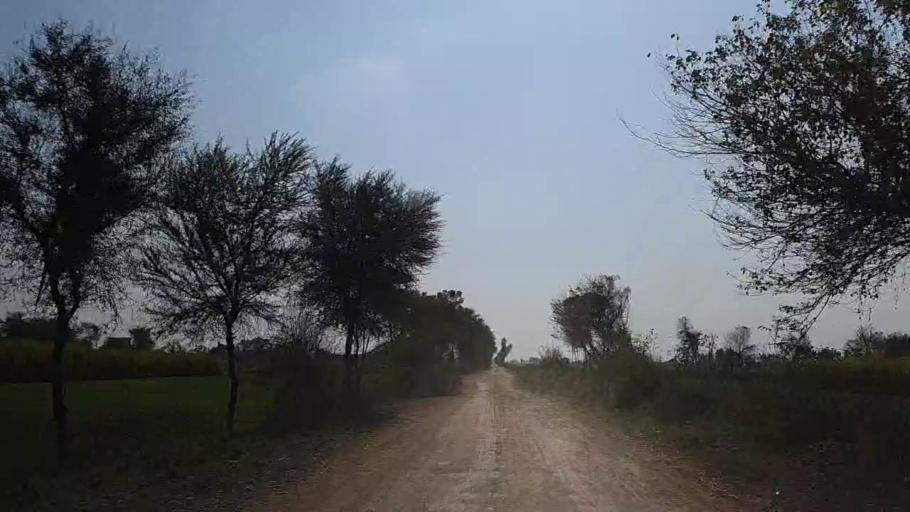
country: PK
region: Sindh
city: Daur
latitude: 26.4608
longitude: 68.2632
